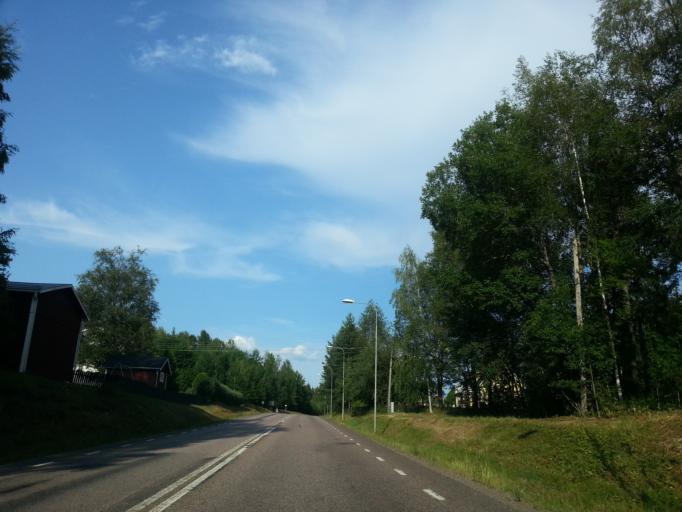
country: SE
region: Vaestmanland
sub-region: Norbergs Kommun
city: Norberg
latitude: 60.0739
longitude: 15.9406
